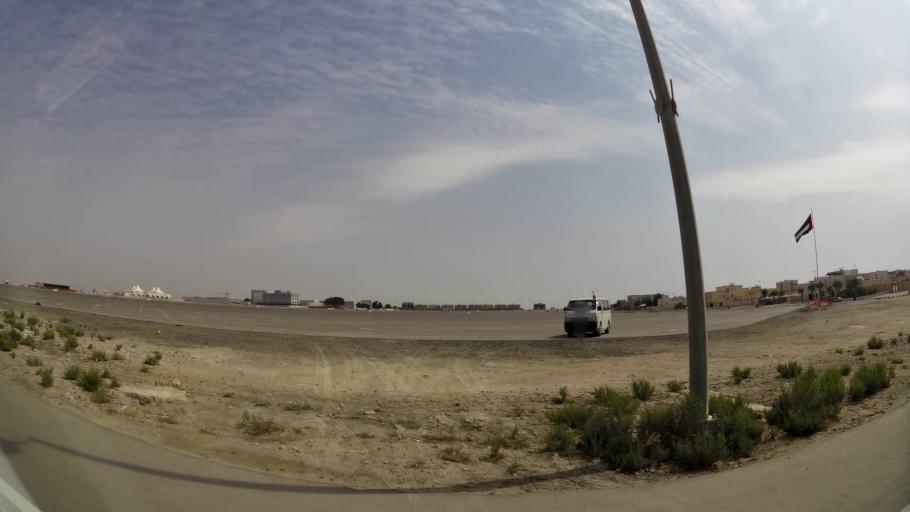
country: AE
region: Abu Dhabi
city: Abu Dhabi
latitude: 24.5348
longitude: 54.6717
